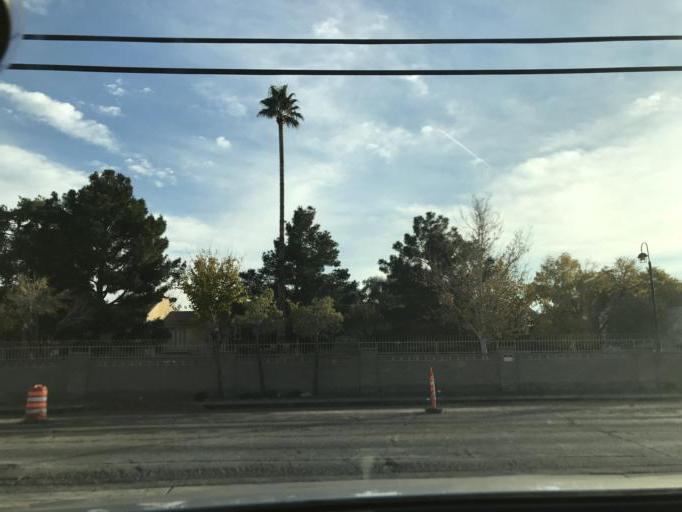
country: US
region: Nevada
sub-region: Clark County
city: Winchester
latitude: 36.1408
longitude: -115.1398
